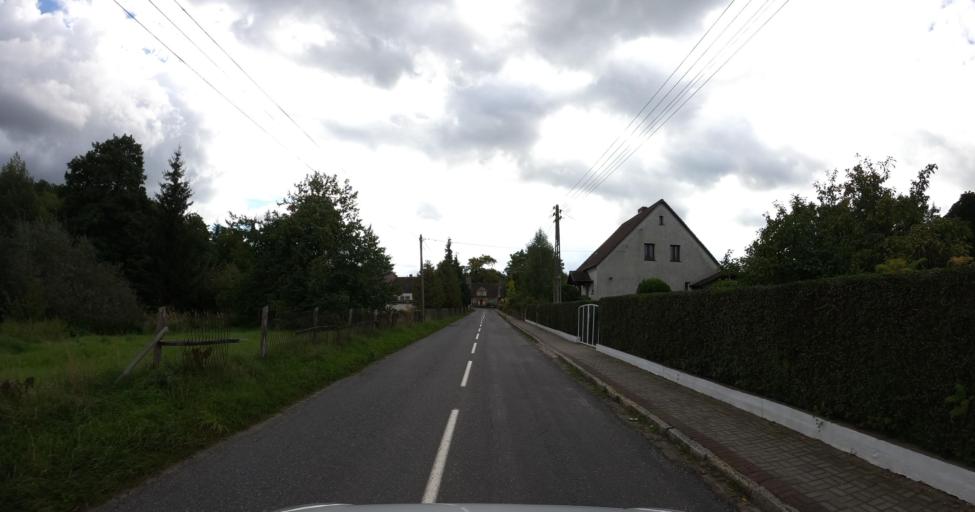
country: PL
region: Lubusz
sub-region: Powiat zielonogorski
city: Zabor
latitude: 51.9604
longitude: 15.6220
